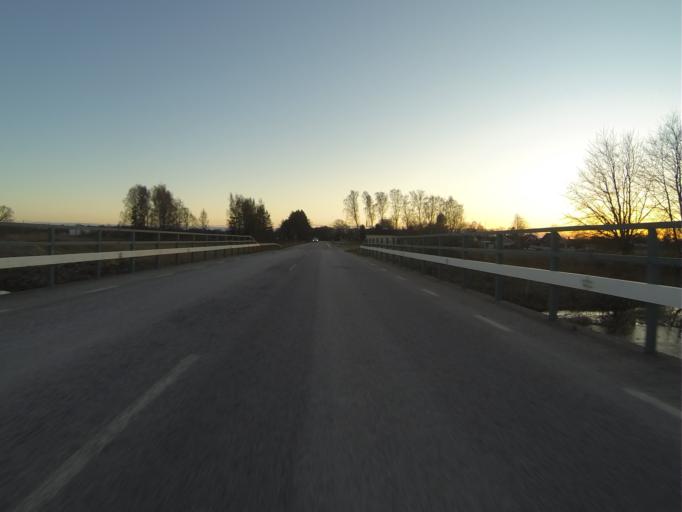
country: SE
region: Skane
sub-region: Hoors Kommun
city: Loberod
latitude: 55.7295
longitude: 13.4680
